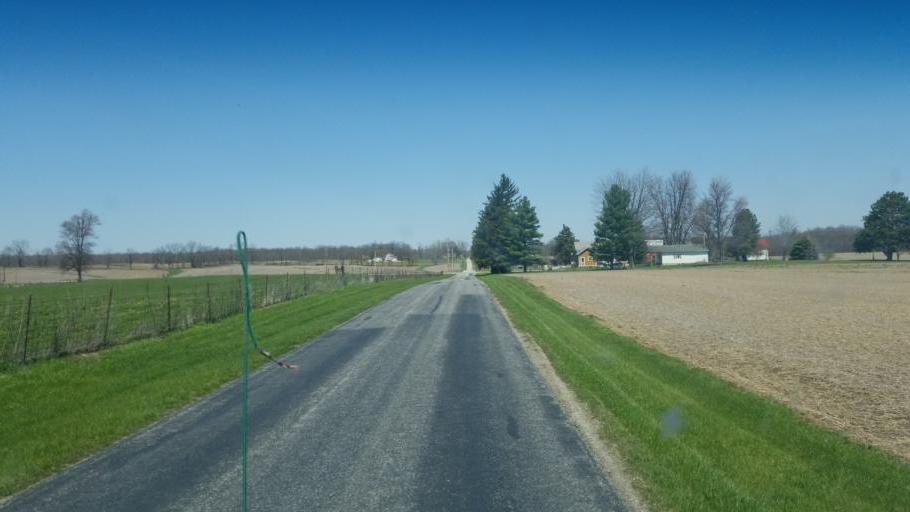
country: US
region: Ohio
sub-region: Huron County
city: New London
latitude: 41.0861
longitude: -82.4379
